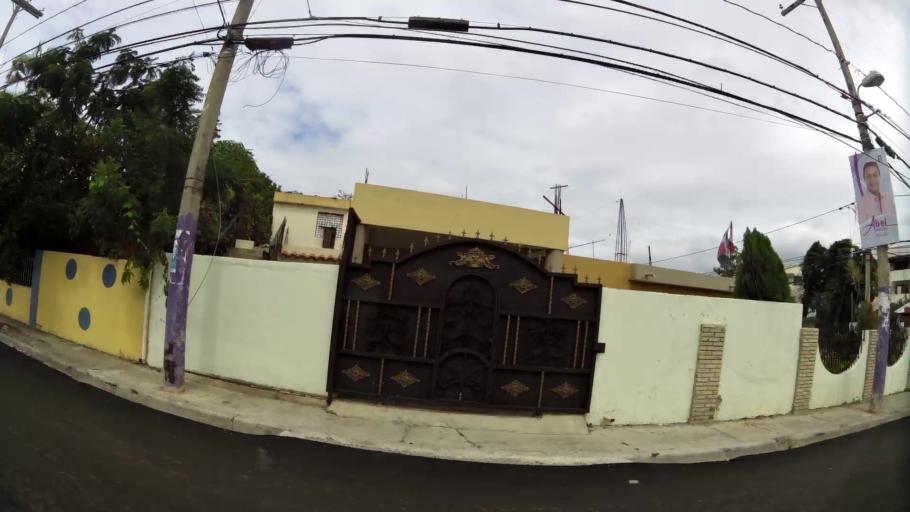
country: DO
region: Santiago
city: Santiago de los Caballeros
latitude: 19.4377
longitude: -70.6705
